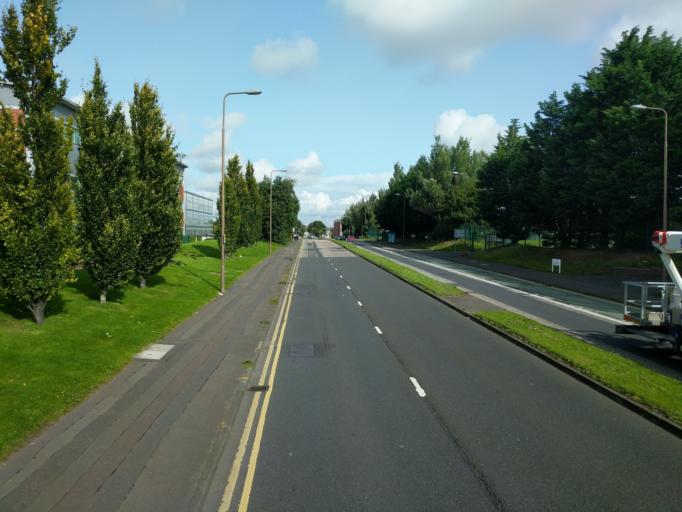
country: GB
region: Scotland
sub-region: Edinburgh
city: Currie
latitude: 55.9302
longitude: -3.2922
